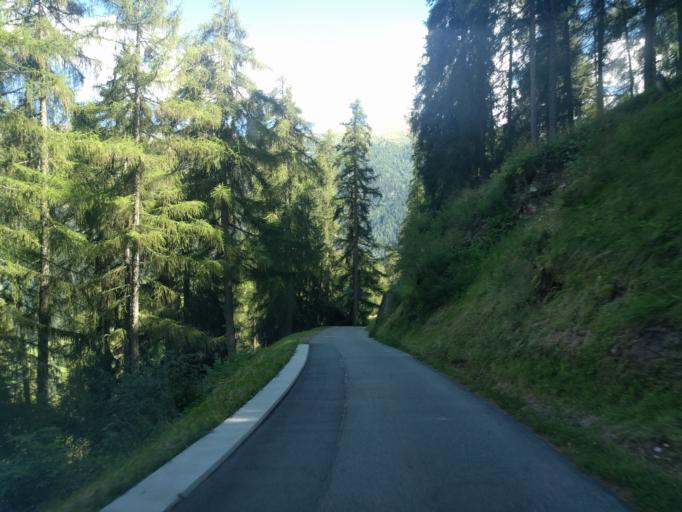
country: IT
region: Trentino-Alto Adige
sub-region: Bolzano
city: Tubre
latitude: 46.6113
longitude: 10.4219
